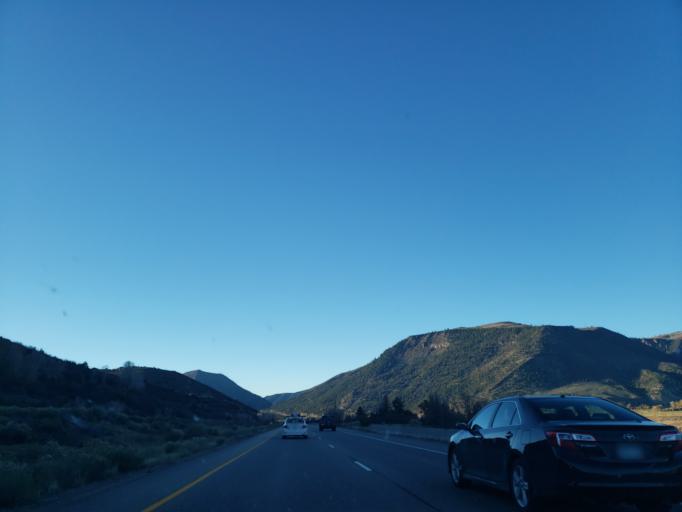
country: US
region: Colorado
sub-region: Pitkin County
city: Snowmass Village
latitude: 39.2780
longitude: -106.8960
